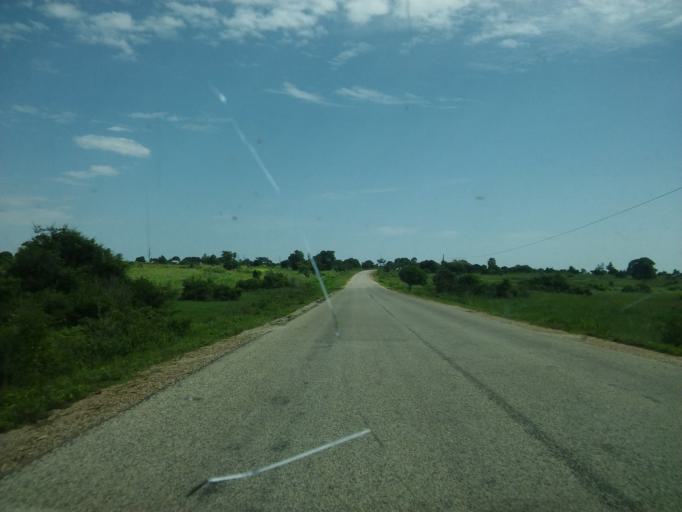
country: UG
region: Eastern Region
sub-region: Bukedea District
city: Bukedea
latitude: 1.3062
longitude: 34.0670
